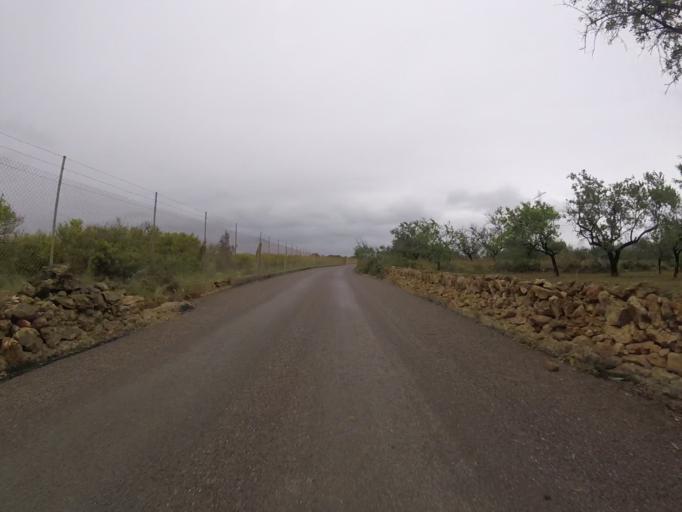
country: ES
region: Valencia
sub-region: Provincia de Castello
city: Alcoceber
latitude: 40.2372
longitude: 0.2525
